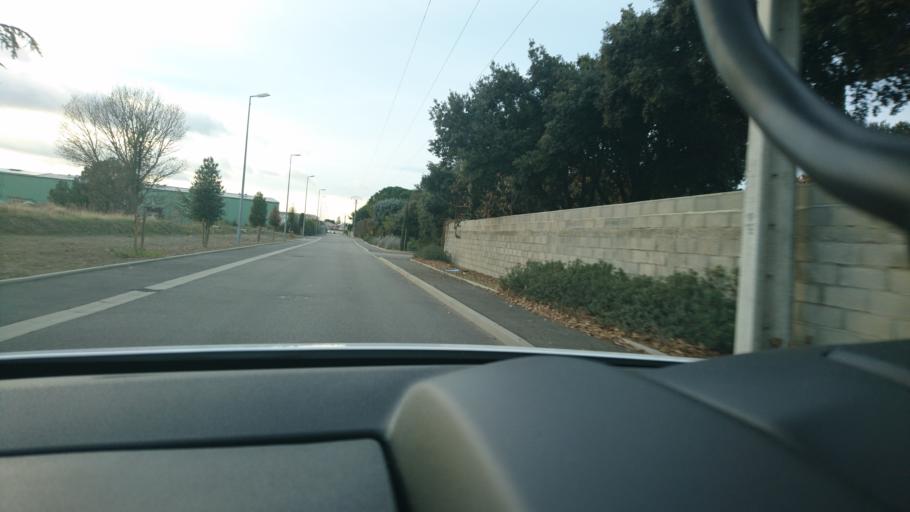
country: FR
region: Provence-Alpes-Cote d'Azur
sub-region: Departement du Vaucluse
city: Bollene
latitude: 44.2837
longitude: 4.7637
